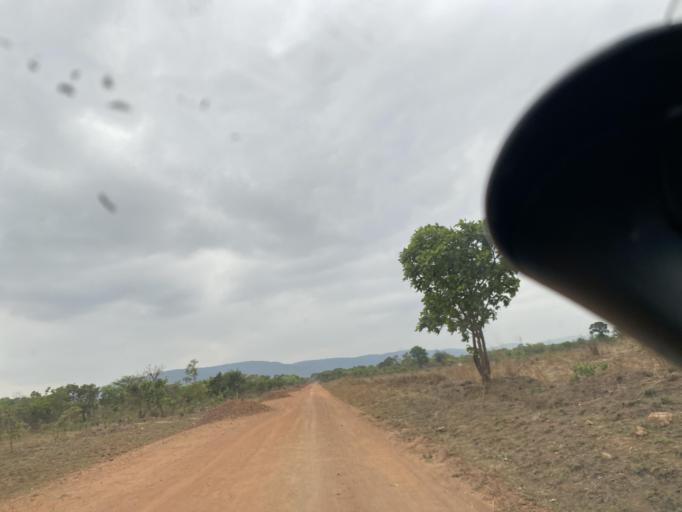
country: ZM
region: Lusaka
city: Chongwe
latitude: -15.2116
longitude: 28.7561
